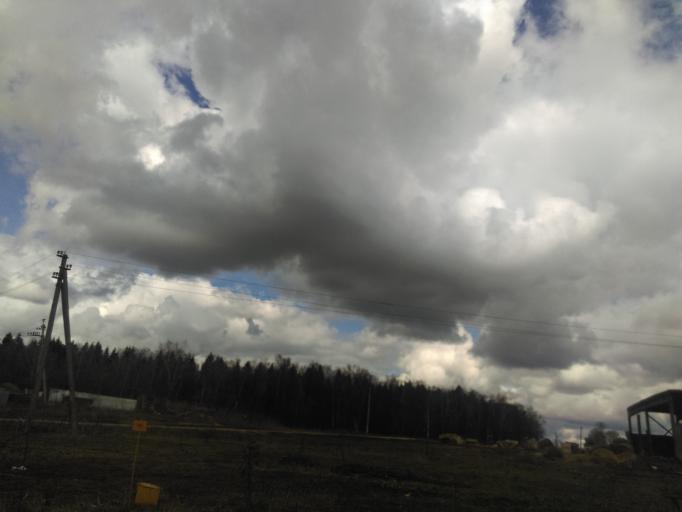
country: RU
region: Moskovskaya
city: Dorokhovo
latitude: 55.6516
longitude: 36.3316
